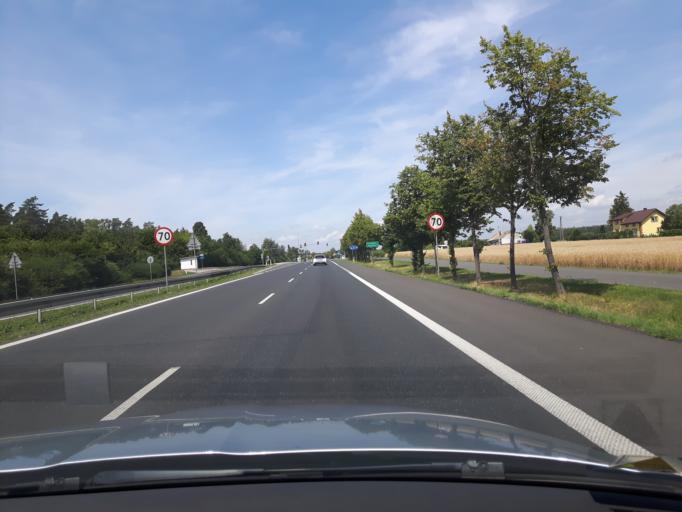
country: PL
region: Masovian Voivodeship
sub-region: Powiat plonski
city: Zaluski
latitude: 52.4965
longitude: 20.5418
